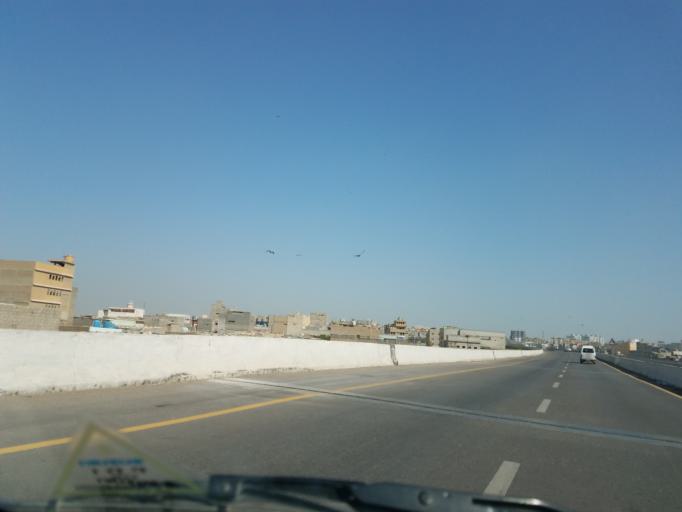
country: PK
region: Sindh
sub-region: Karachi District
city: Karachi
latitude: 24.8810
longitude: 67.0073
